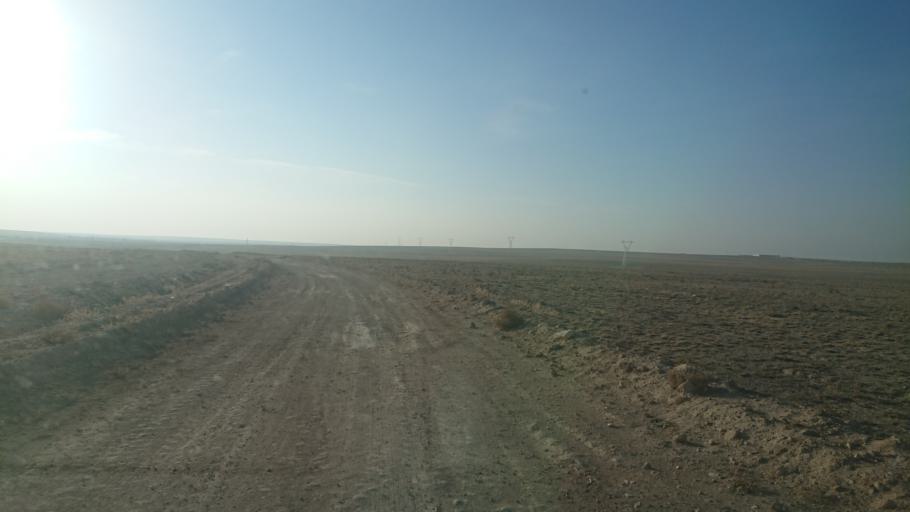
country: TR
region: Aksaray
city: Sultanhani
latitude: 38.1441
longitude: 33.5782
